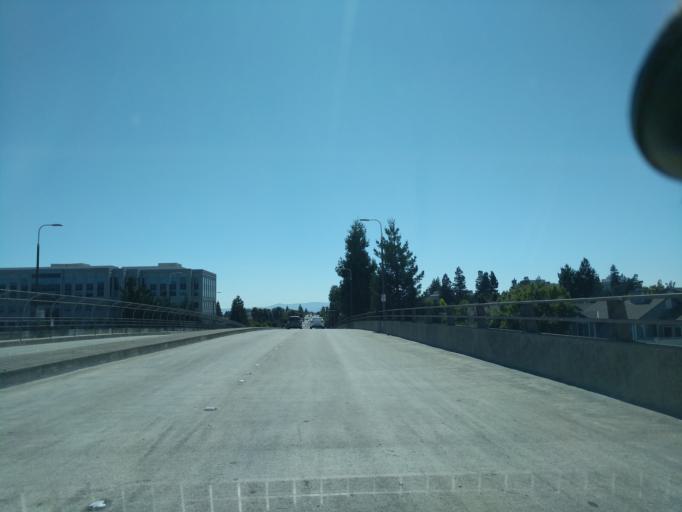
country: US
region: California
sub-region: Alameda County
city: Hayward
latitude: 37.6600
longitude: -122.0925
